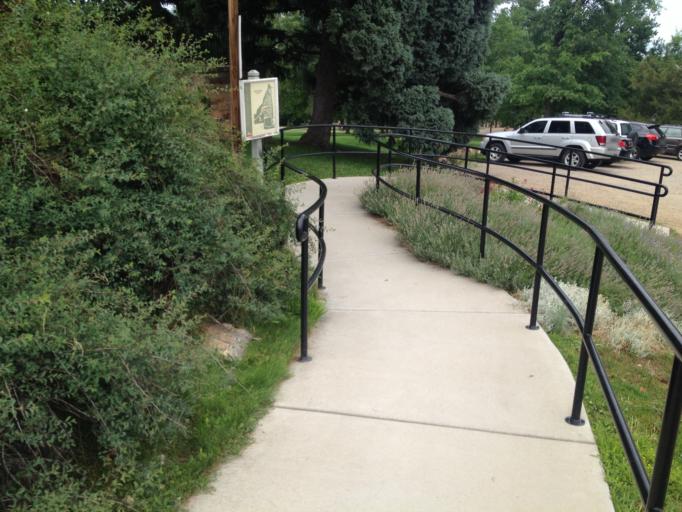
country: US
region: Colorado
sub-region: Boulder County
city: Boulder
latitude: 39.9978
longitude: -105.2798
